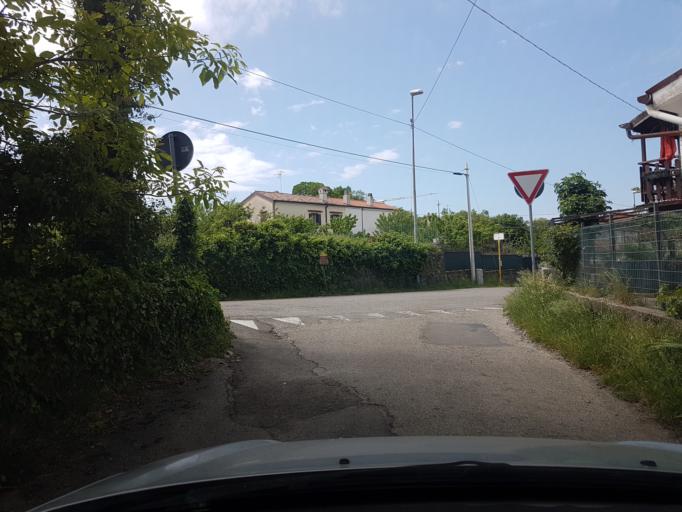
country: IT
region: Friuli Venezia Giulia
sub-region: Provincia di Trieste
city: Sistiana-Visogliano
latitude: 45.7856
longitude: 13.6580
